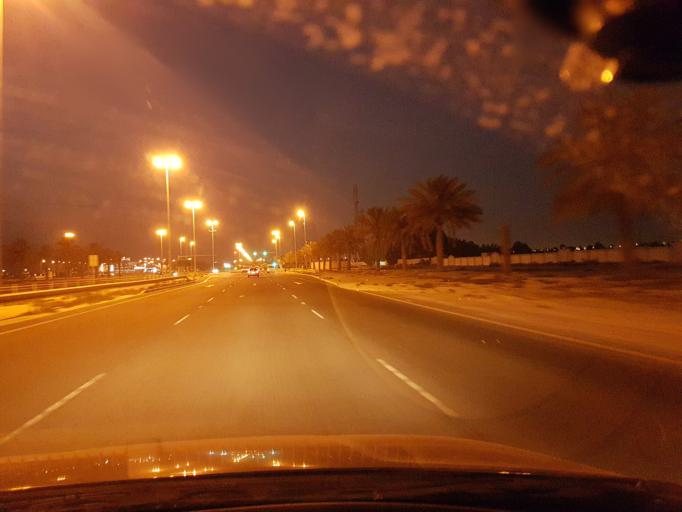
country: BH
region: Central Governorate
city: Dar Kulayb
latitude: 26.0459
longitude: 50.5000
